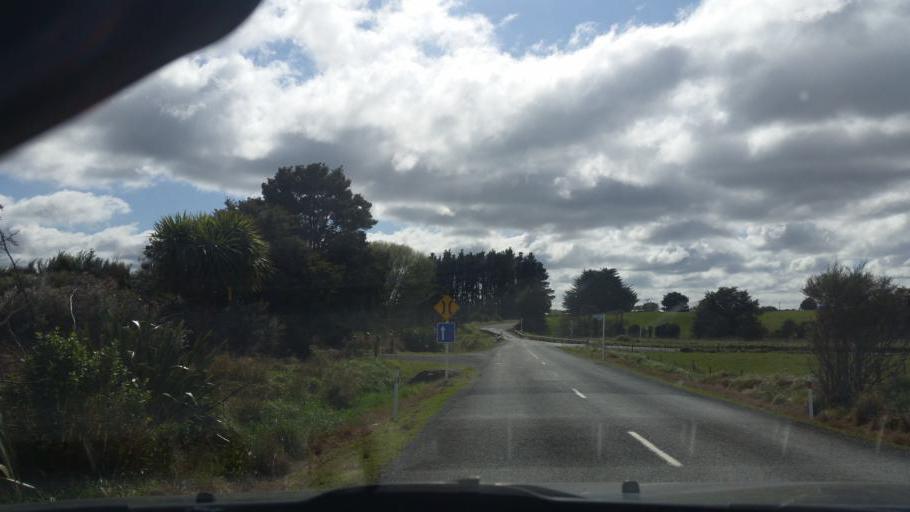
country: NZ
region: Auckland
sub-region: Auckland
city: Wellsford
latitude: -36.1491
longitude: 174.5034
